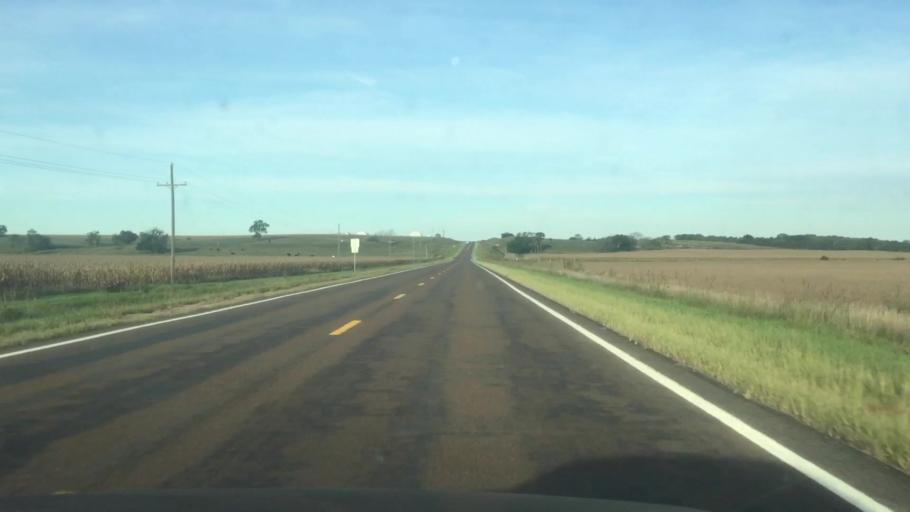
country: US
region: Nebraska
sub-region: Gage County
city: Wymore
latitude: 40.0457
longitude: -96.8174
